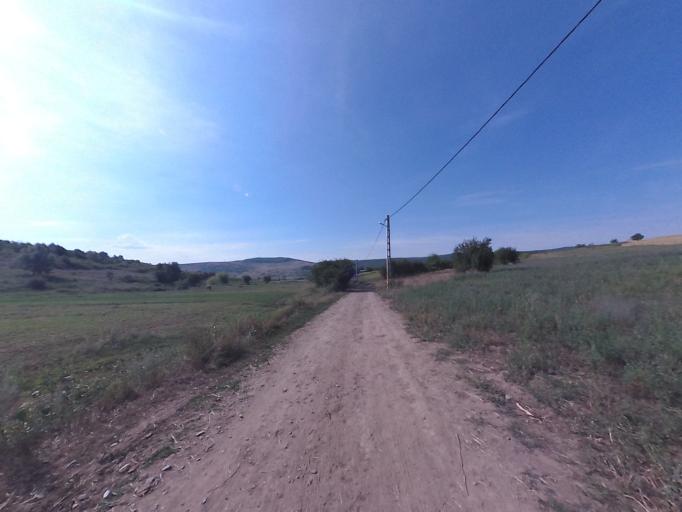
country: RO
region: Vaslui
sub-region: Comuna Osesti
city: Buda
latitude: 46.7681
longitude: 27.4303
